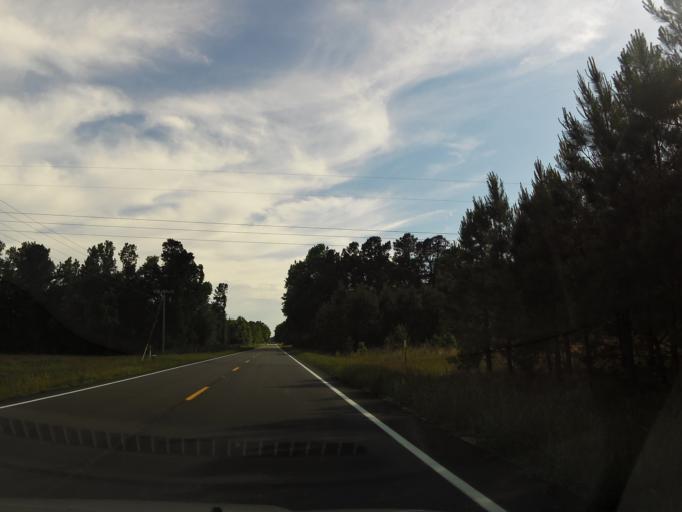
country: US
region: South Carolina
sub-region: Allendale County
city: Fairfax
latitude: 32.9805
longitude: -81.2278
